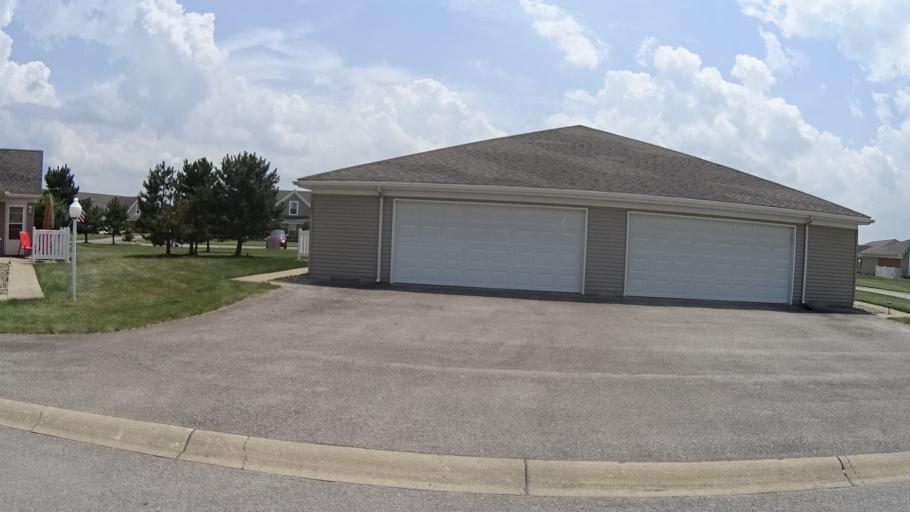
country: US
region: Ohio
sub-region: Lorain County
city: Vermilion
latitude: 41.4090
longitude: -82.3707
